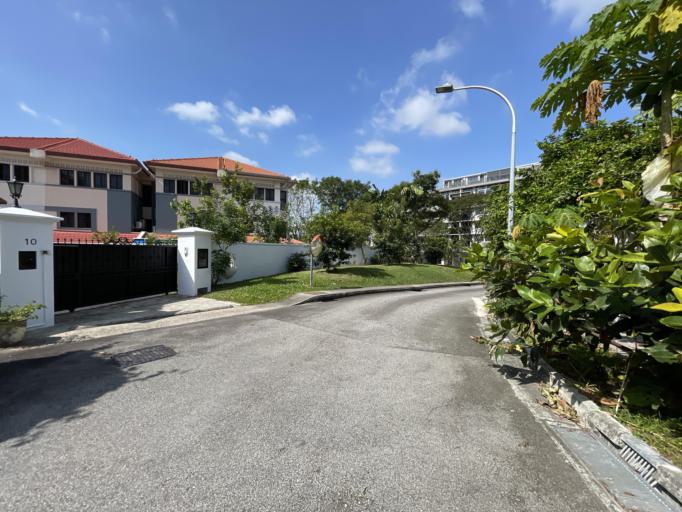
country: SG
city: Singapore
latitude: 1.2796
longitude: 103.7867
